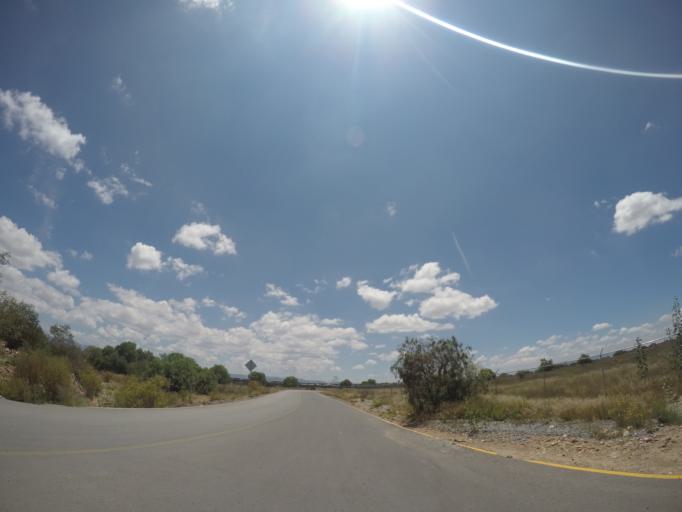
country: MX
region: San Luis Potosi
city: La Pila
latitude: 22.0225
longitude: -100.8990
